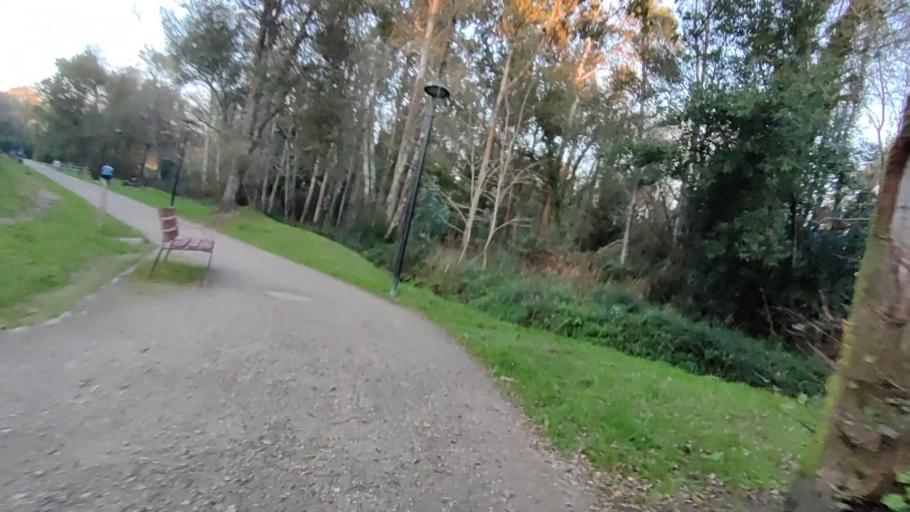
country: ES
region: Galicia
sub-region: Provincia da Coruna
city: Boiro
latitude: 42.6417
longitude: -8.8795
